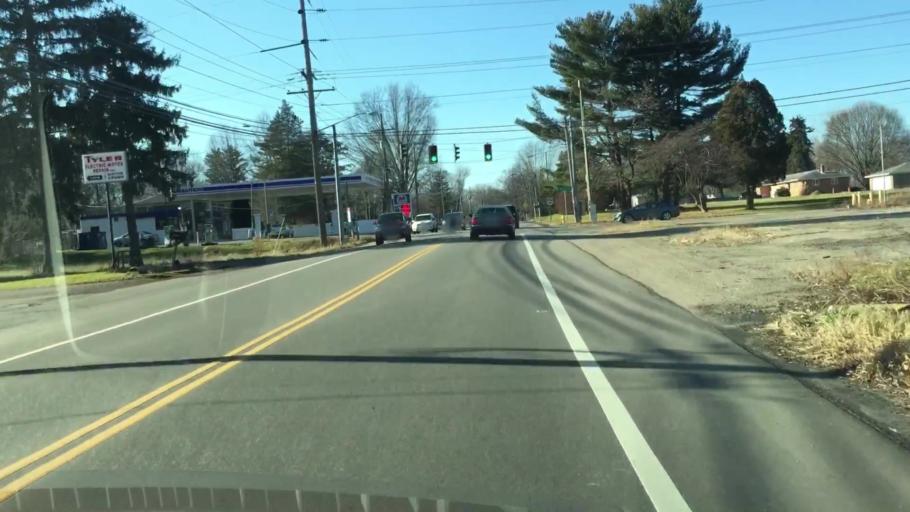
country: US
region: Ohio
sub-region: Summit County
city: Fairlawn
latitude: 41.0835
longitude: -81.5895
